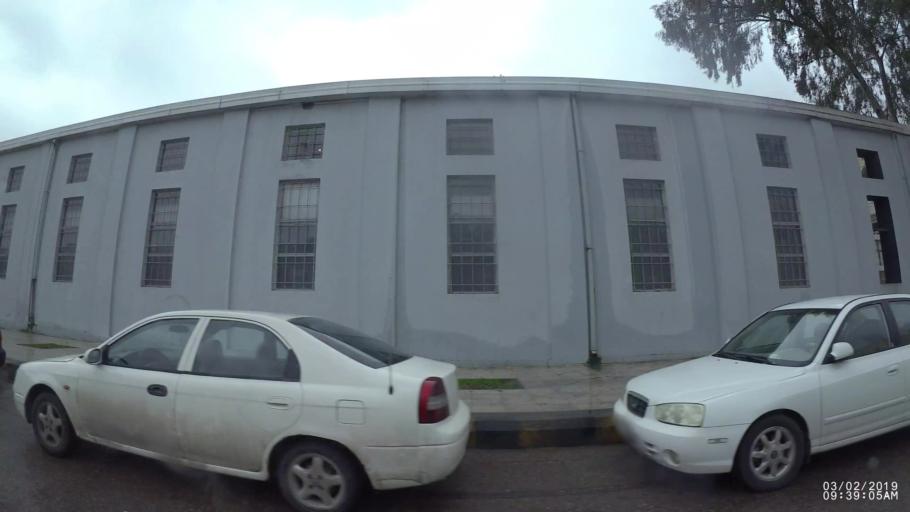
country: JO
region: Amman
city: Amman
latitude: 31.9444
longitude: 35.9216
